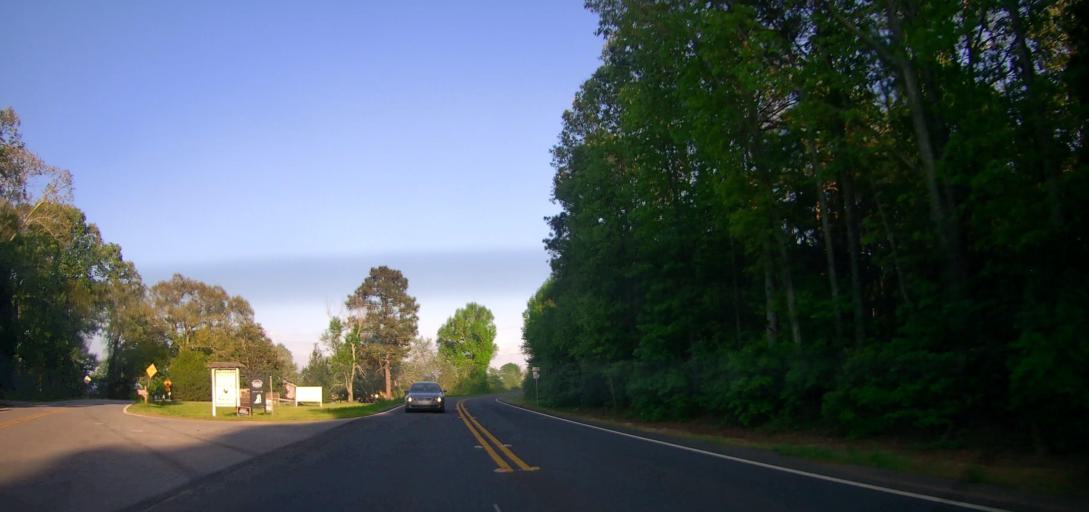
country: US
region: Georgia
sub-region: Walton County
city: Social Circle
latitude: 33.5051
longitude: -83.6562
